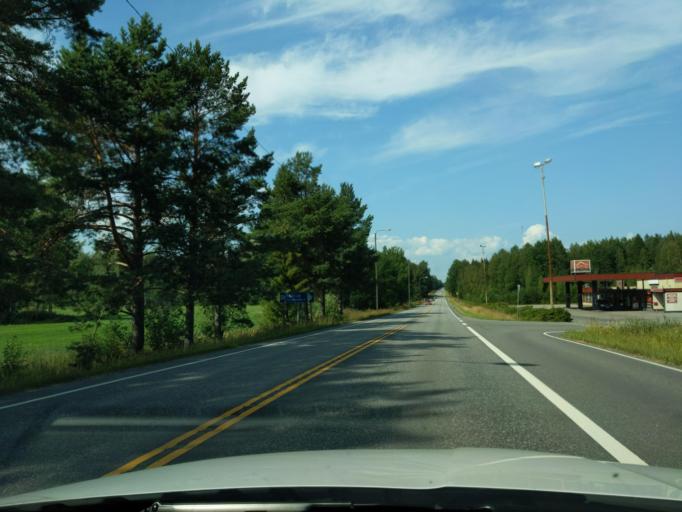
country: FI
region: Paijanne Tavastia
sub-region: Lahti
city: Padasjoki
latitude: 61.3521
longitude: 25.2304
